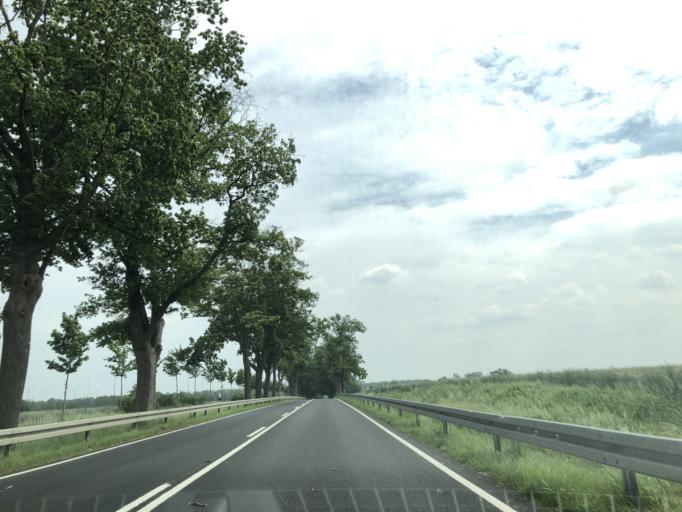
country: DE
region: Brandenburg
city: Gumtow
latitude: 52.9762
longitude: 12.2653
